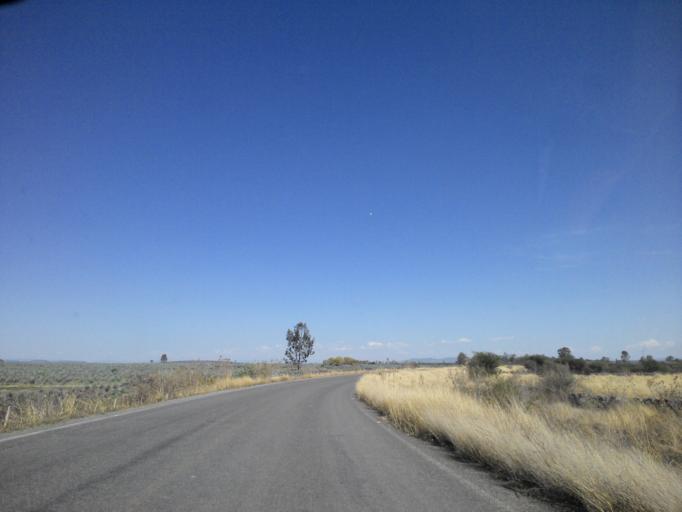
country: MX
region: Jalisco
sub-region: Arandas
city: Santiaguito (Santiaguito de Velazquez)
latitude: 20.8269
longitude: -102.1575
